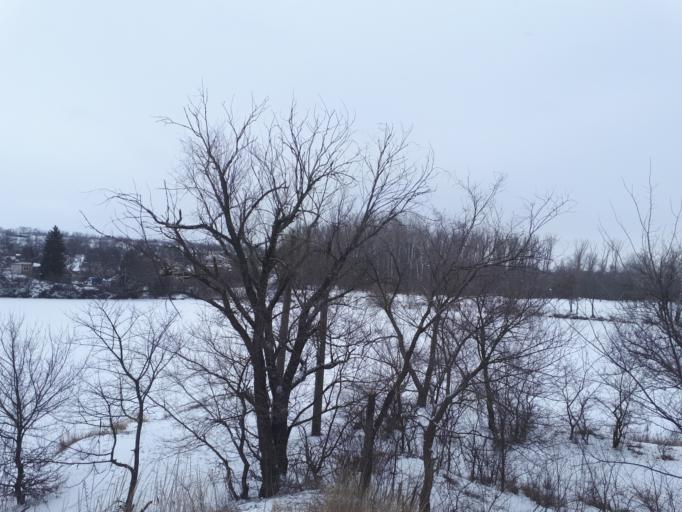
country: RU
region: Rostov
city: Krasnyy Sulin
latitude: 47.9053
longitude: 40.0466
